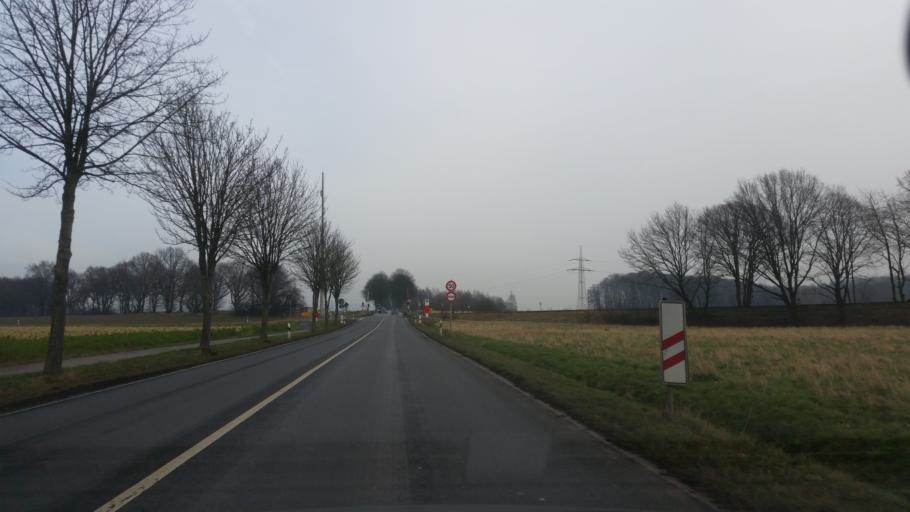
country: DE
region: North Rhine-Westphalia
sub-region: Regierungsbezirk Detmold
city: Lage
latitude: 52.0039
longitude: 8.8313
